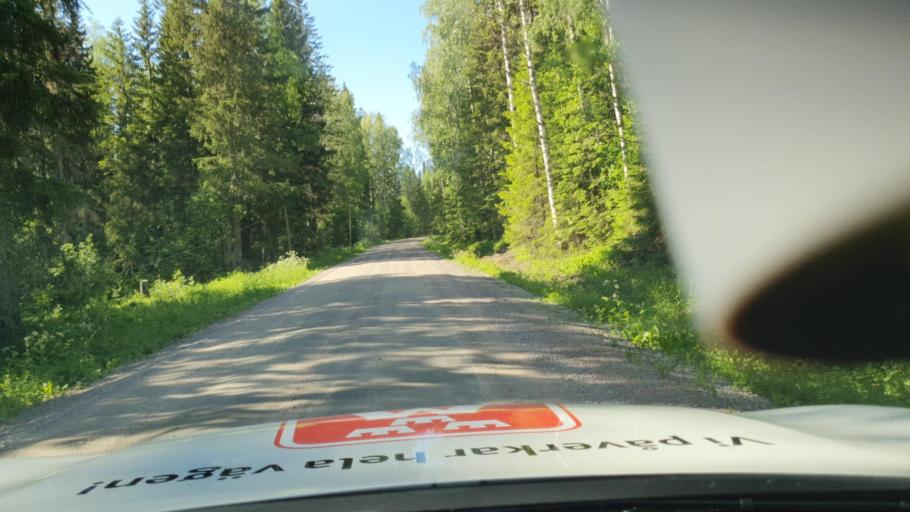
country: SE
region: Vaesterbotten
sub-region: Vannas Kommun
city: Vaennaes
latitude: 63.7861
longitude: 19.6262
